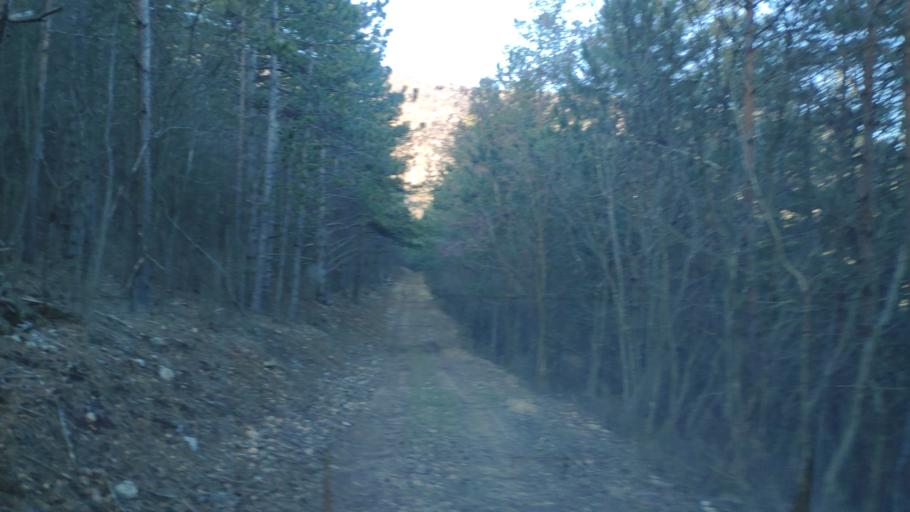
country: SK
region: Kosicky
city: Medzev
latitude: 48.6078
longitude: 20.7384
